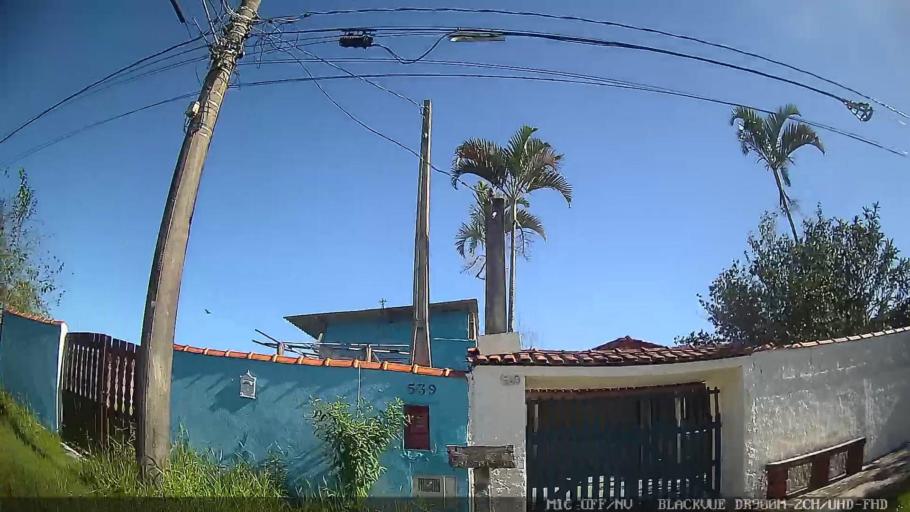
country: BR
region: Sao Paulo
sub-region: Itanhaem
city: Itanhaem
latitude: -24.2084
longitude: -46.8513
